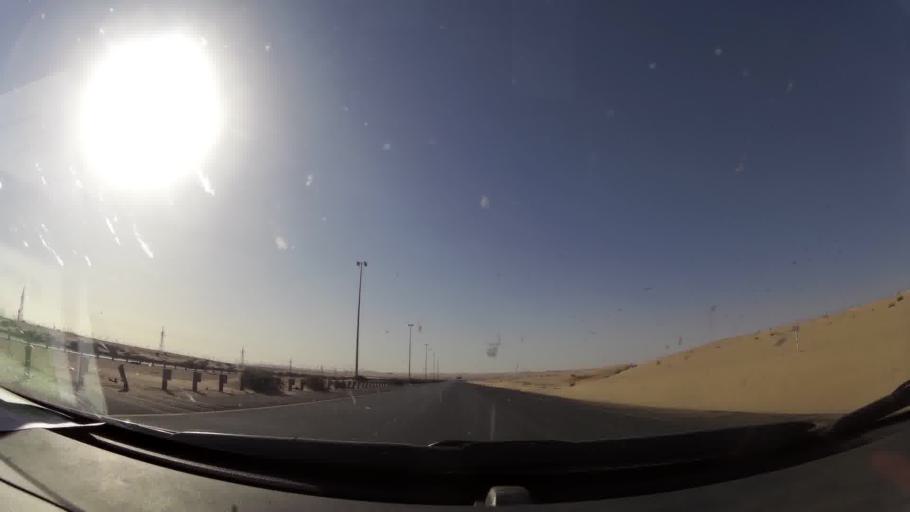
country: KW
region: Al Asimah
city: Kuwait City
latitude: 29.6452
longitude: 47.9525
